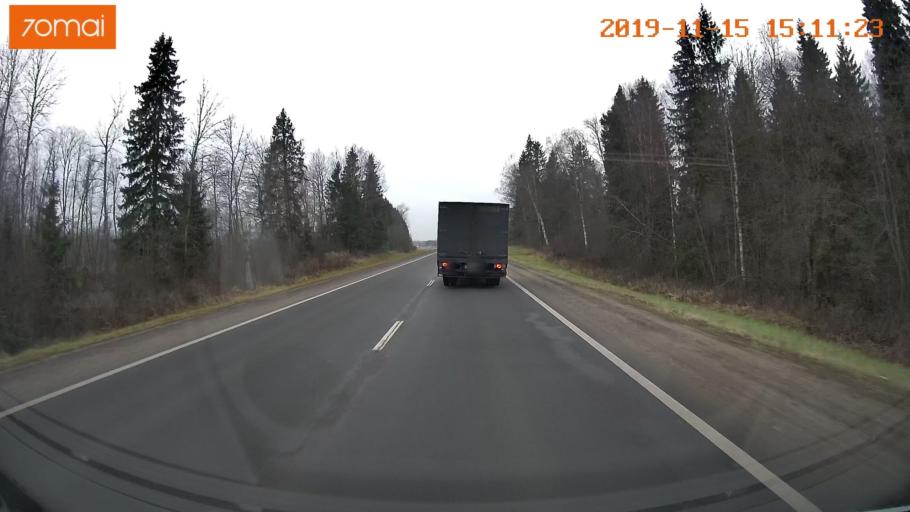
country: RU
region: Jaroslavl
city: Prechistoye
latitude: 58.3369
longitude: 40.2415
